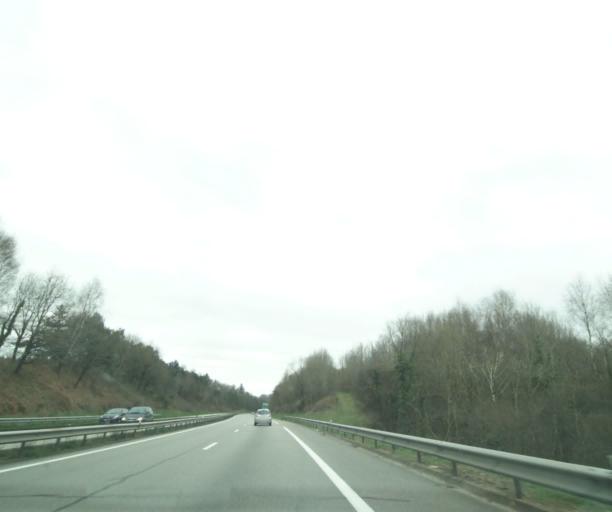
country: FR
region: Limousin
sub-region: Departement de la Haute-Vienne
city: Bonnac-la-Cote
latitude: 45.9313
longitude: 1.3030
